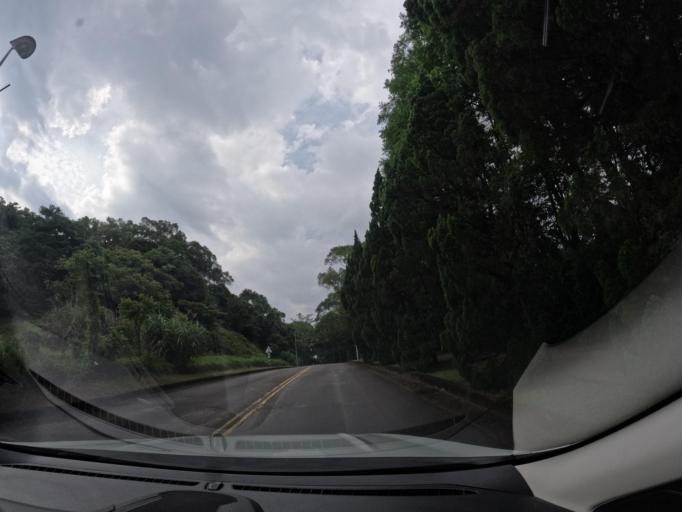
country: TW
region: Taiwan
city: Daxi
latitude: 24.8845
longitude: 121.3236
